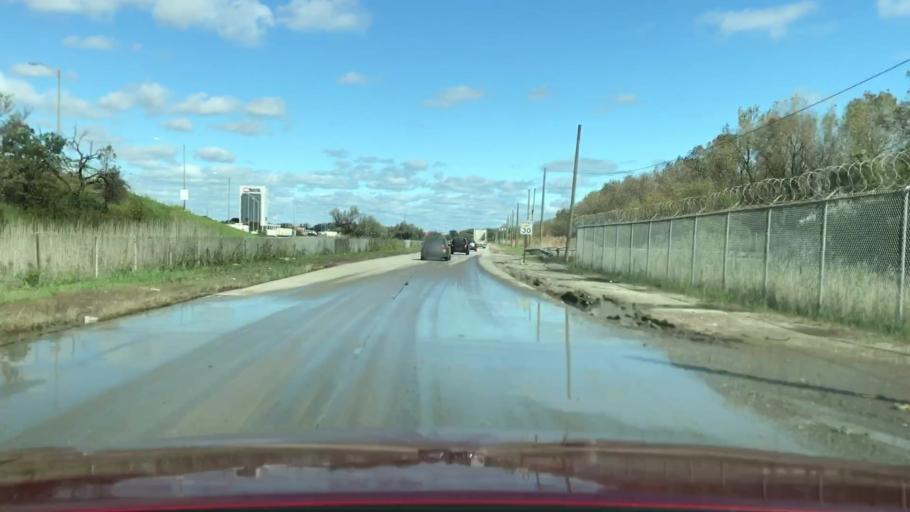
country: US
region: Illinois
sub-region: Cook County
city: Dolton
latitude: 41.6856
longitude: -87.6006
